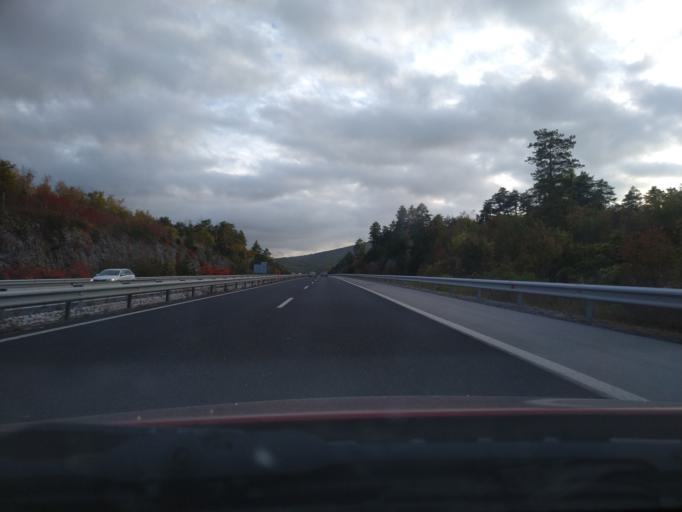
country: SI
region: Divaca
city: Divaca
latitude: 45.6607
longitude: 13.9643
